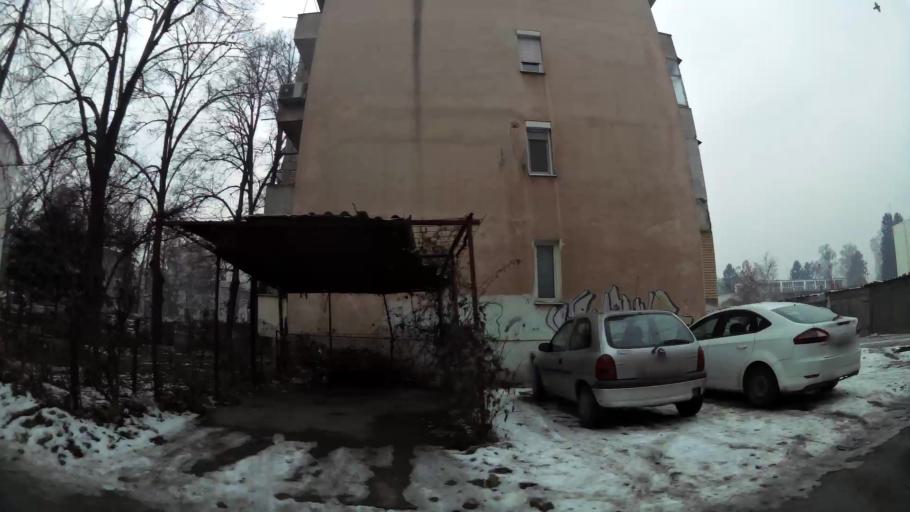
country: MK
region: Cair
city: Cair
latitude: 42.0056
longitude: 21.4655
